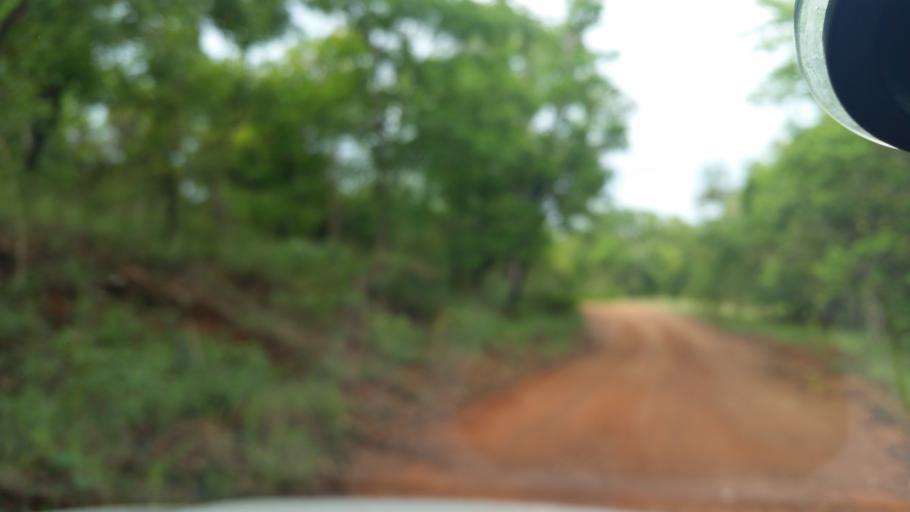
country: BR
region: Goias
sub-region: Porangatu
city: Porangatu
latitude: -13.9791
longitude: -49.2694
